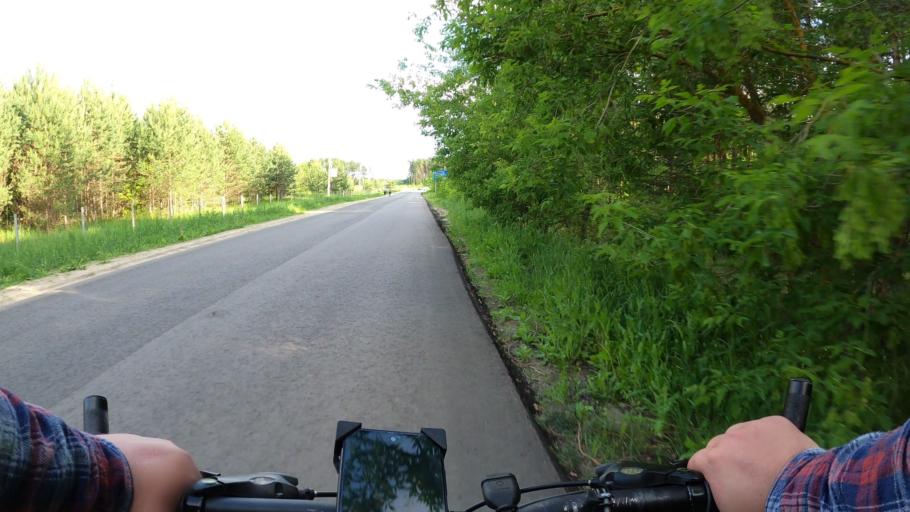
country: RU
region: Moskovskaya
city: Ashitkovo
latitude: 55.4372
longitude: 38.6333
